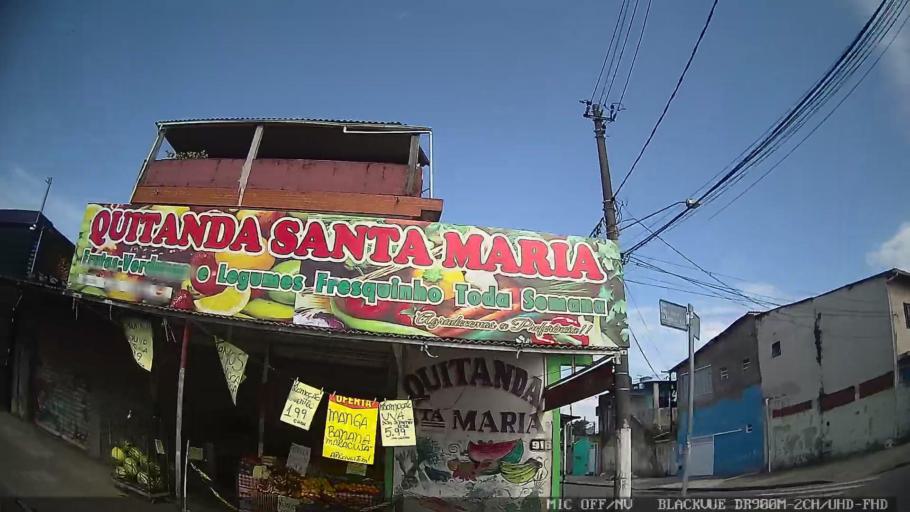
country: BR
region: Sao Paulo
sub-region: Guaruja
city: Guaruja
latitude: -23.9540
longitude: -46.2822
